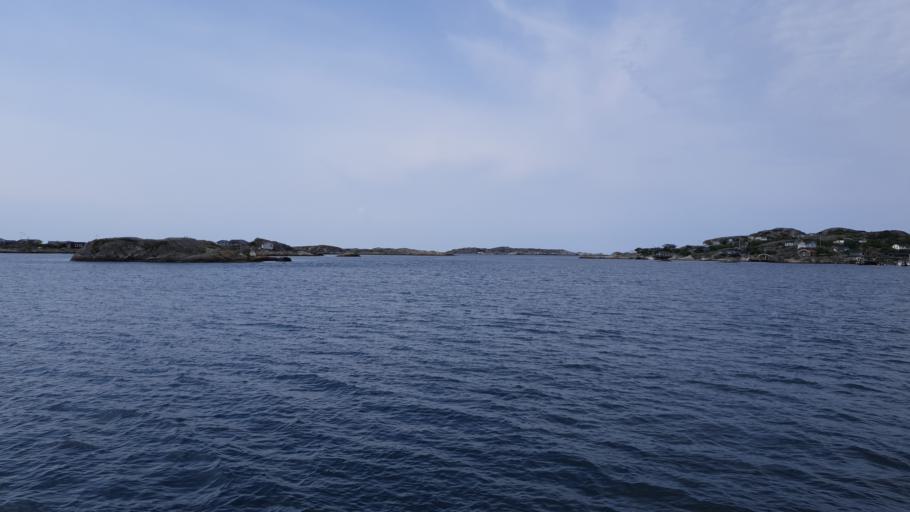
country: SE
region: Vaestra Goetaland
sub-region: Goteborg
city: Styrso
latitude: 57.5948
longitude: 11.7752
